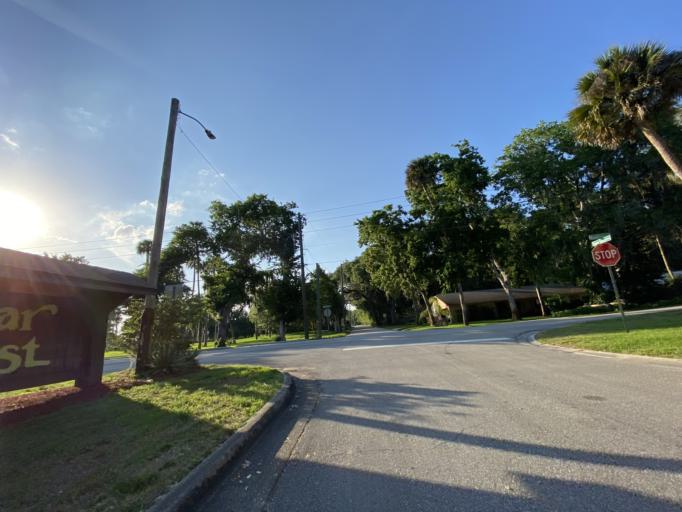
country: US
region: Florida
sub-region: Volusia County
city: Port Orange
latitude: 29.1468
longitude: -81.0086
